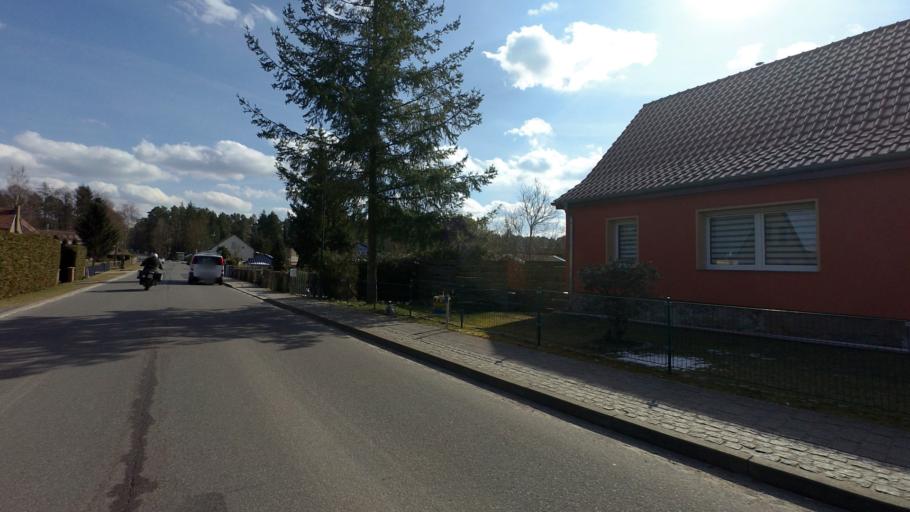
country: DE
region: Brandenburg
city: Marienwerder
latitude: 52.8088
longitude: 13.5843
